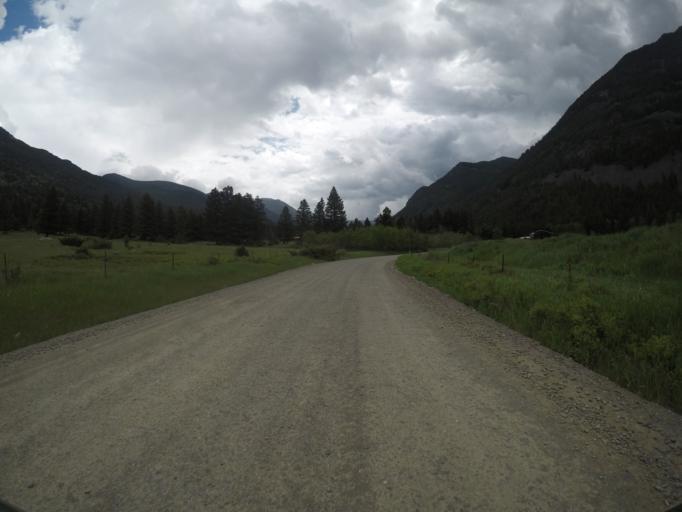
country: US
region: Montana
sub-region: Park County
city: Livingston
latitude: 45.4845
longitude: -110.2113
